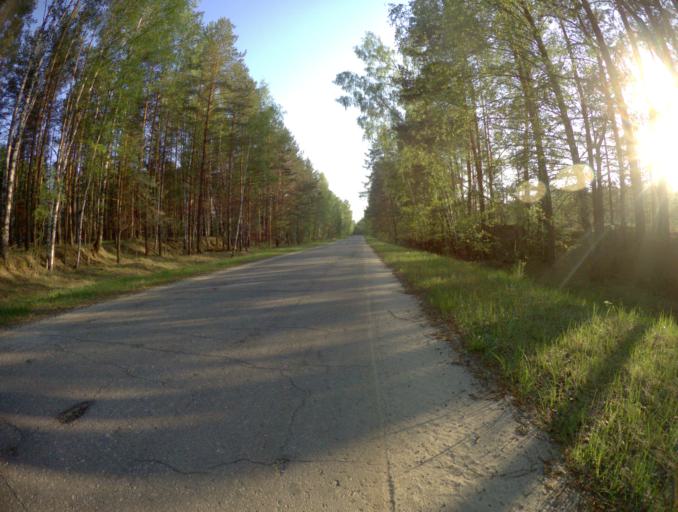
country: RU
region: Vladimir
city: Vyazniki
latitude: 56.3332
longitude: 42.1278
